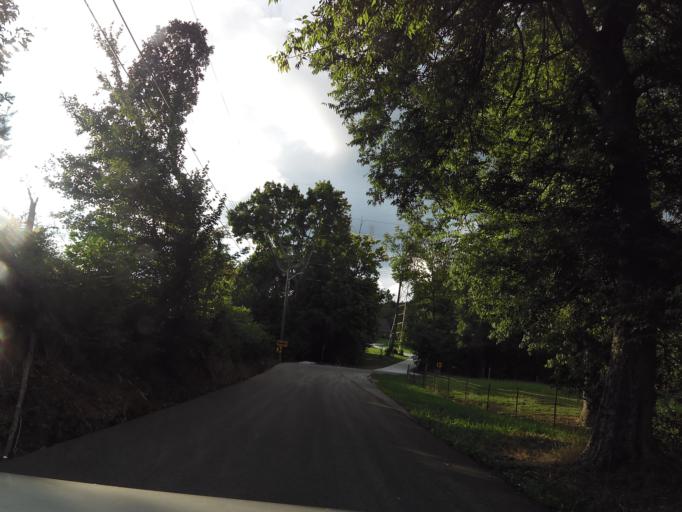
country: US
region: Tennessee
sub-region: Knox County
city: Knoxville
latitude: 36.0006
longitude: -84.0126
